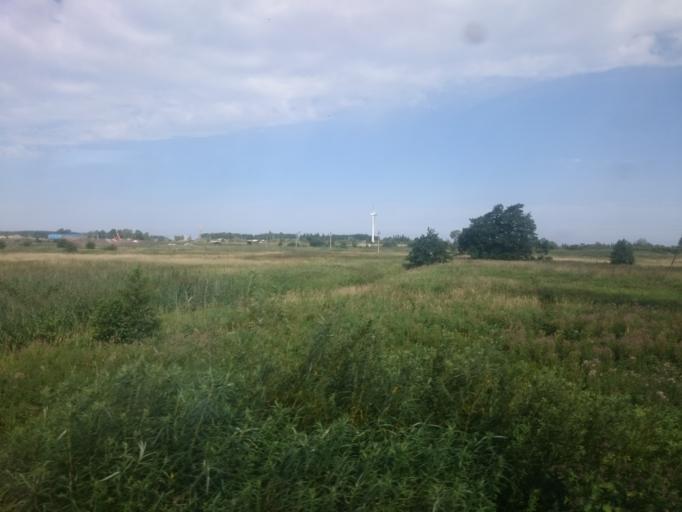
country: RU
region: Kaliningrad
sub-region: Zelenogradskiy Rayon
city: Zelenogradsk
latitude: 54.9304
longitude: 20.3763
